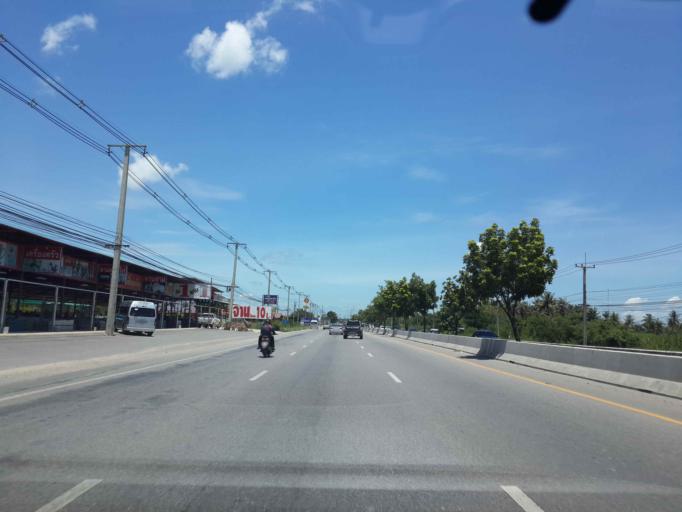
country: TH
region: Phetchaburi
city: Cha-am
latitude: 12.8602
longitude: 99.9219
